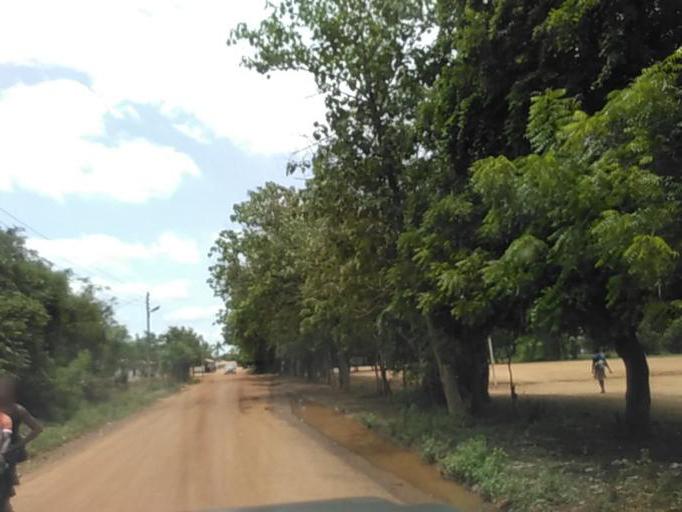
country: GH
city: Akropong
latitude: 6.0293
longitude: 0.3736
